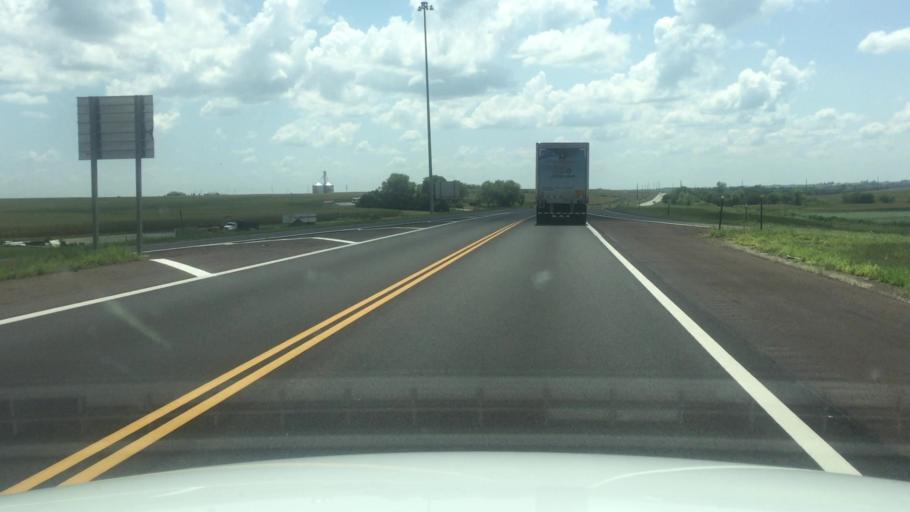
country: US
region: Kansas
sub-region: Nemaha County
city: Sabetha
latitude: 39.8379
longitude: -95.7352
